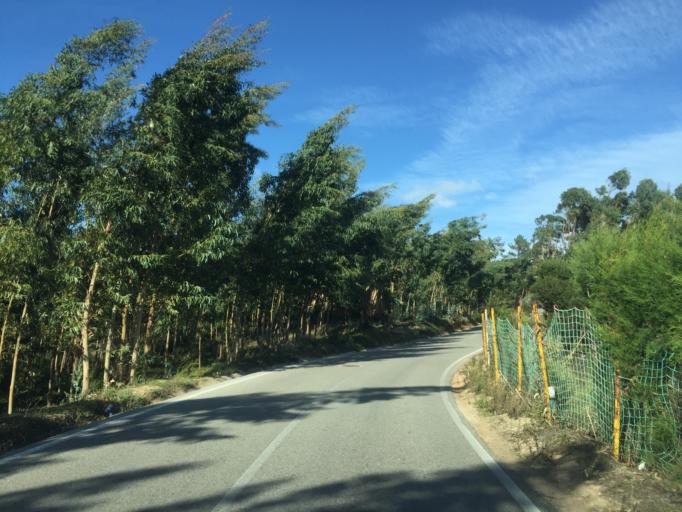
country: PT
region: Coimbra
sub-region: Figueira da Foz
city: Tavarede
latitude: 40.1766
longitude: -8.8382
